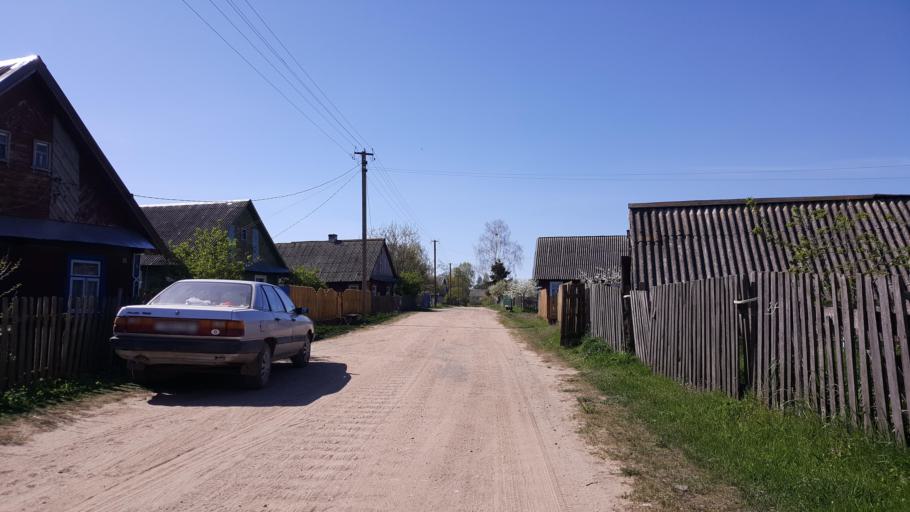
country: BY
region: Brest
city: Kamyanyets
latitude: 52.4546
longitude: 23.8817
